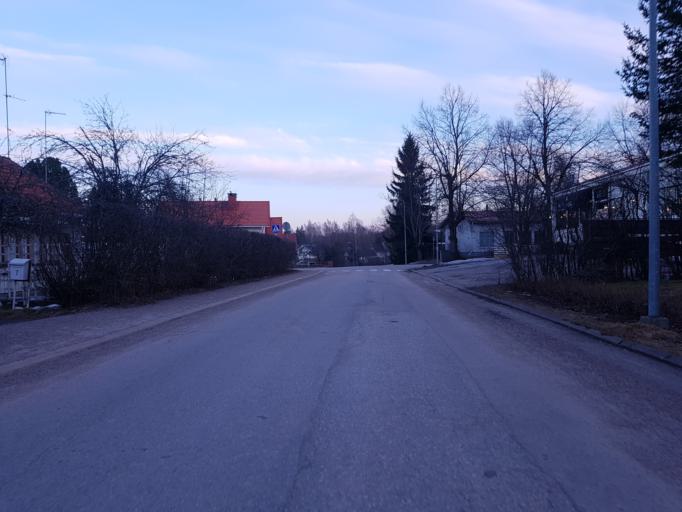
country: FI
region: Uusimaa
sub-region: Helsinki
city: Vantaa
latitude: 60.2605
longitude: 24.9555
